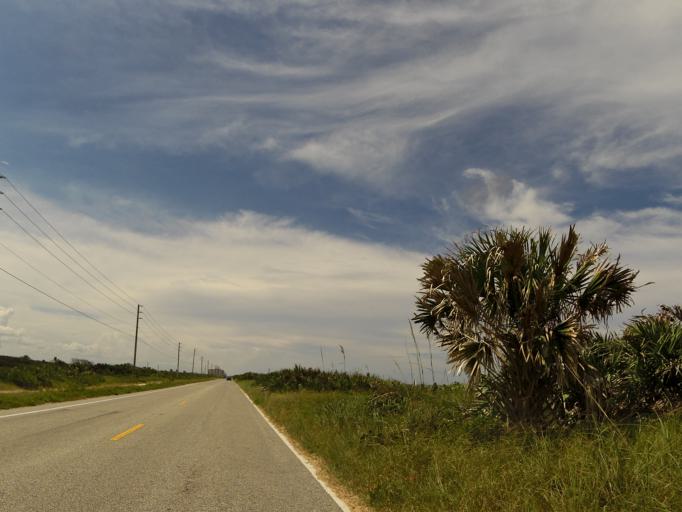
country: US
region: Florida
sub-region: Flagler County
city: Flagler Beach
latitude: 29.4143
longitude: -81.0968
